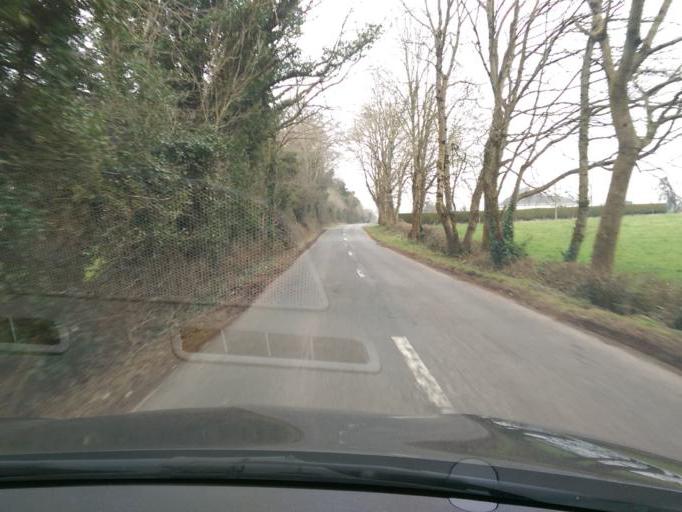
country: IE
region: Leinster
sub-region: An Longfort
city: Lanesborough
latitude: 53.6394
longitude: -7.8875
